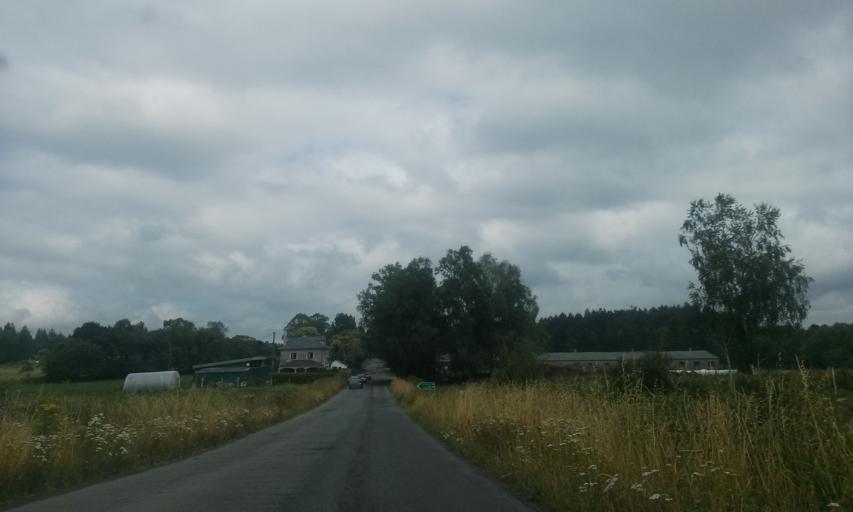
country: ES
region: Galicia
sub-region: Provincia de Lugo
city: Friol
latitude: 43.0907
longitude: -7.8095
